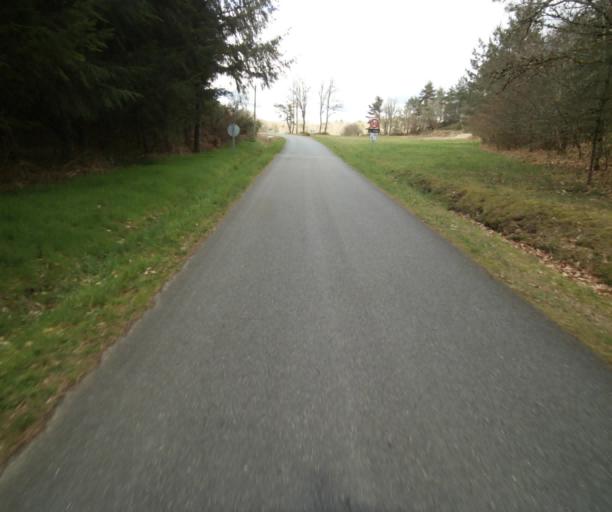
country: FR
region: Limousin
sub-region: Departement de la Correze
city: Correze
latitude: 45.3096
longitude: 1.9331
